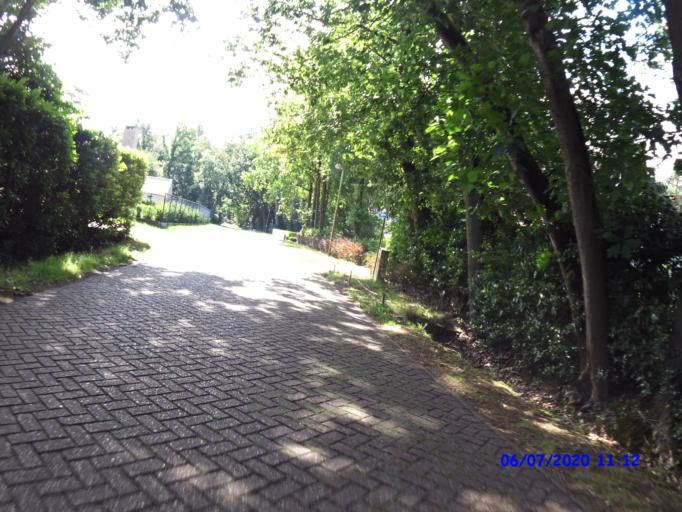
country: BE
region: Flanders
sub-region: Provincie Antwerpen
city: Oud-Turnhout
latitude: 51.3001
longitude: 5.0093
